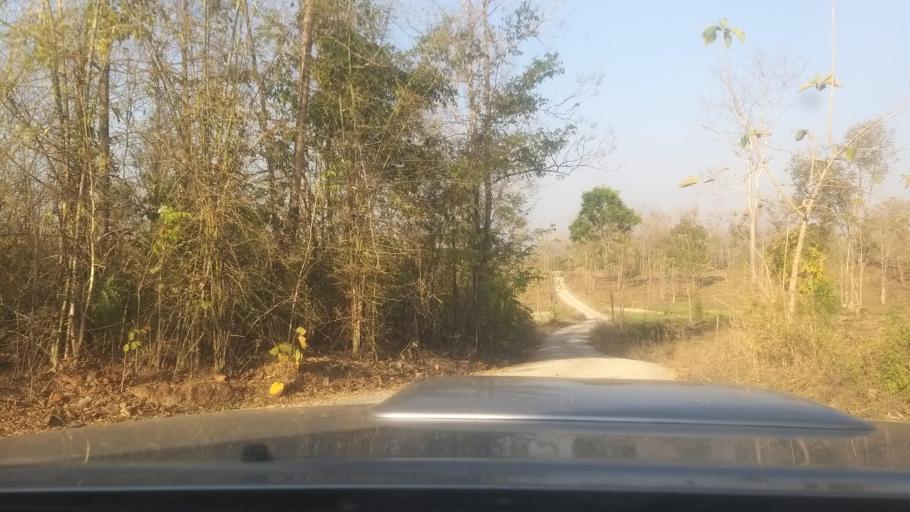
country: TH
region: Phrae
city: Phrae
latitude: 18.2650
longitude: 100.0189
